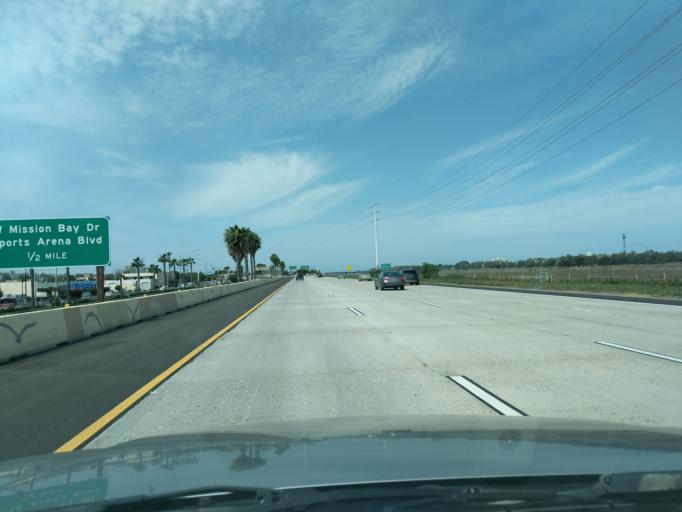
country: US
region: California
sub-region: San Diego County
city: San Diego
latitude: 32.7592
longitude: -117.2096
